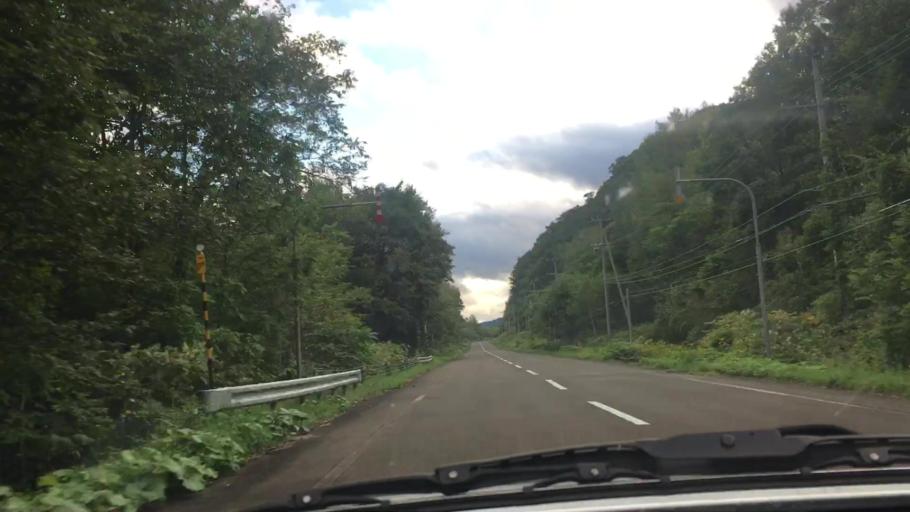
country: JP
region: Hokkaido
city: Shimo-furano
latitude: 43.0201
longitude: 142.4325
